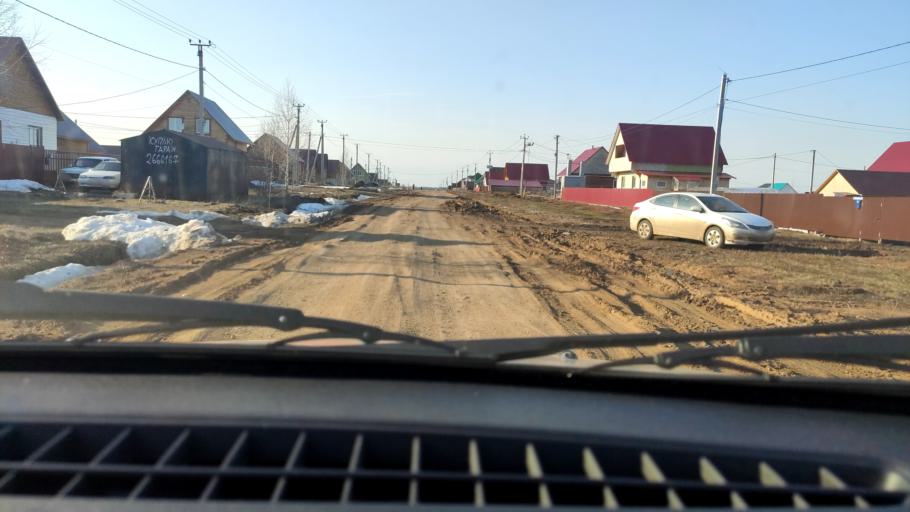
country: RU
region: Bashkortostan
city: Iglino
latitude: 54.8195
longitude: 56.4430
